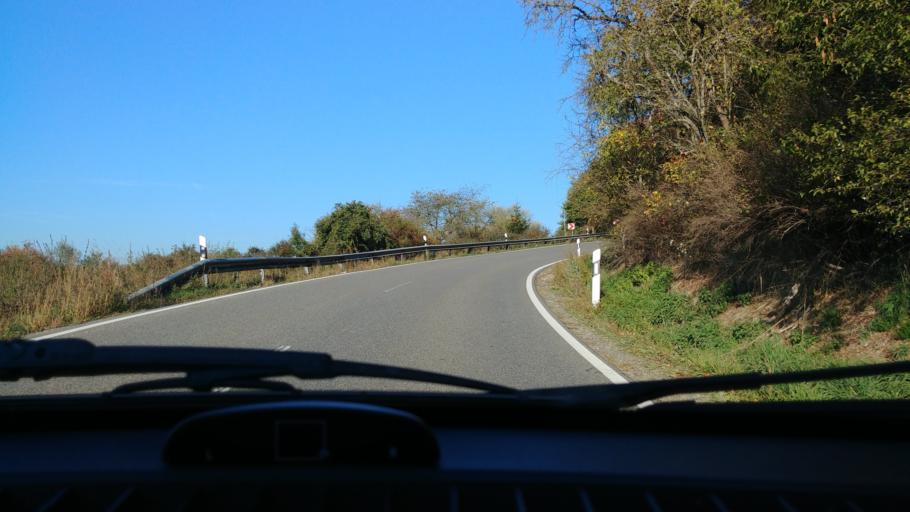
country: DE
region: Rheinland-Pfalz
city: Miehlen
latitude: 50.2339
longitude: 7.8301
